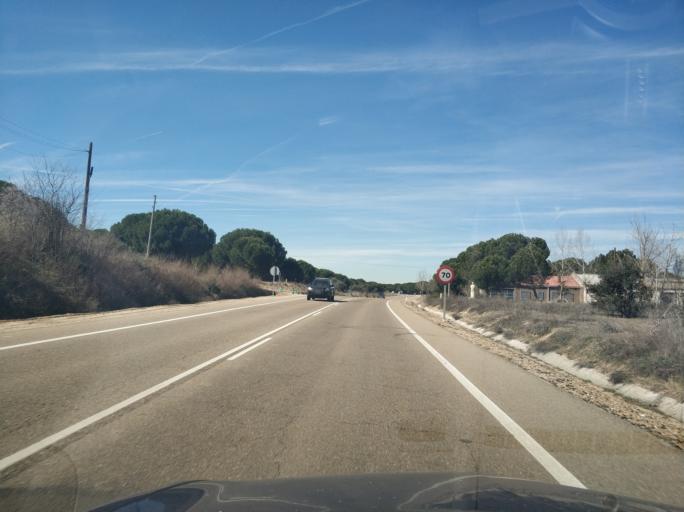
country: ES
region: Castille and Leon
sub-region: Provincia de Valladolid
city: Viana de Cega
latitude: 41.5375
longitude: -4.7656
